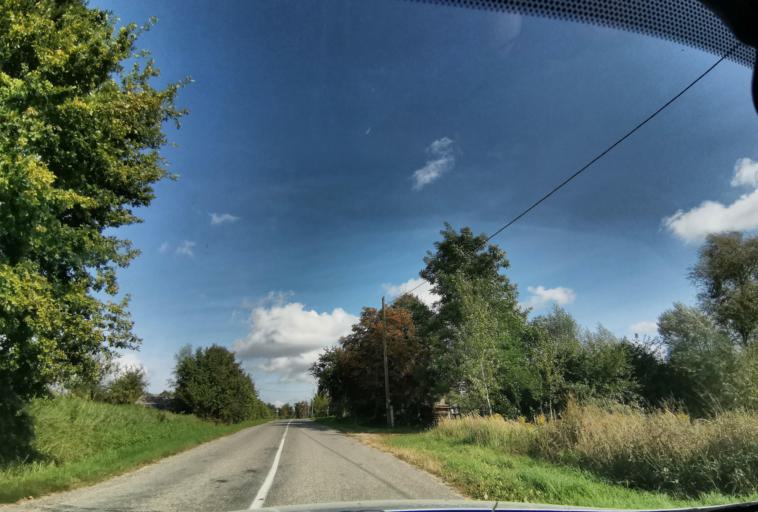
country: RU
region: Kaliningrad
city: Gusev
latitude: 54.6501
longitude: 22.0608
